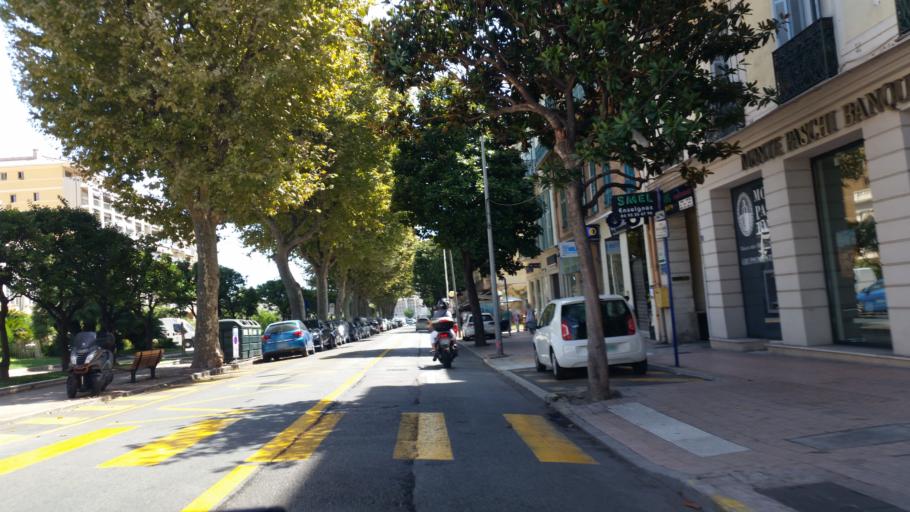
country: FR
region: Provence-Alpes-Cote d'Azur
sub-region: Departement des Alpes-Maritimes
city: Menton
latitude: 43.7744
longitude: 7.4965
